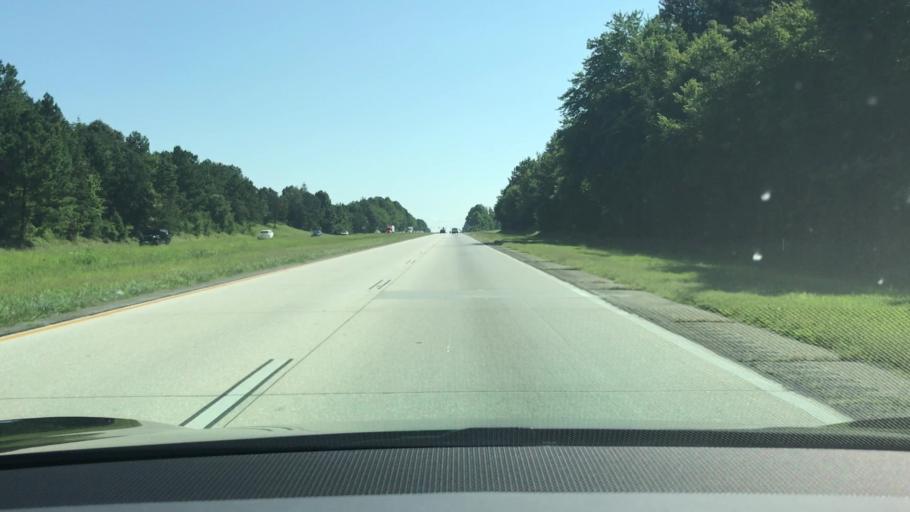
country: US
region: Georgia
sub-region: Hall County
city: Lula
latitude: 34.3899
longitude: -83.6998
